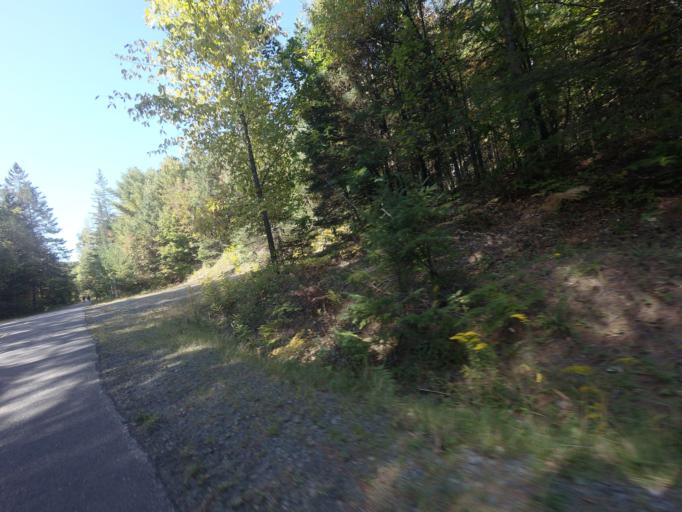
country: CA
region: Quebec
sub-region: Laurentides
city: Mont-Tremblant
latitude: 46.1289
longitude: -74.5784
